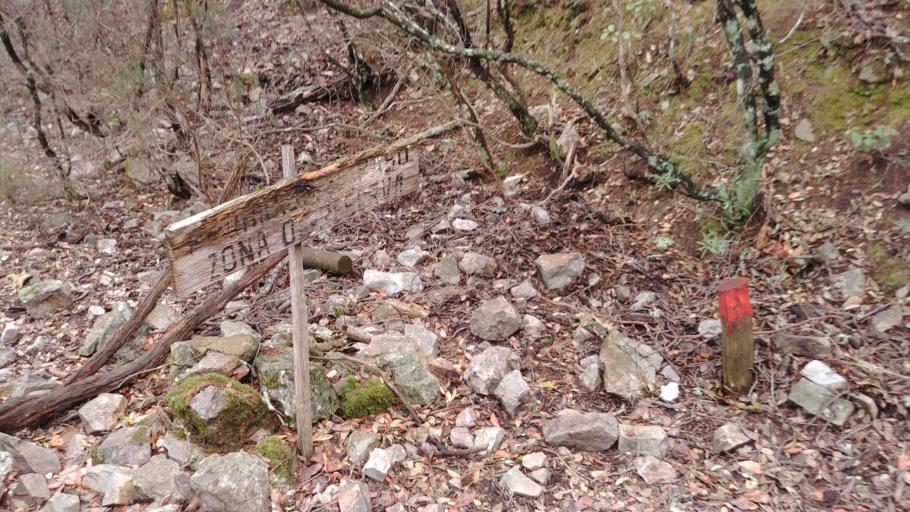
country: ES
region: Extremadura
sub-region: Provincia de Caceres
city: Torrejon el Rubio
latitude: 39.8280
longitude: -6.0309
